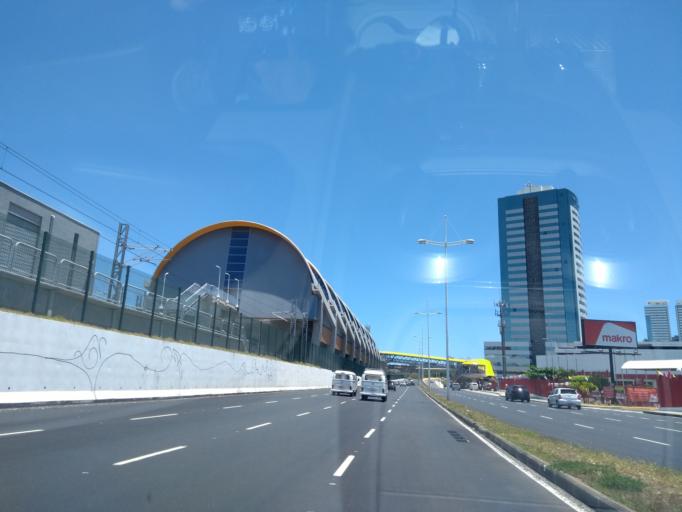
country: BR
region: Bahia
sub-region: Salvador
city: Salvador
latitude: -12.9757
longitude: -38.4591
